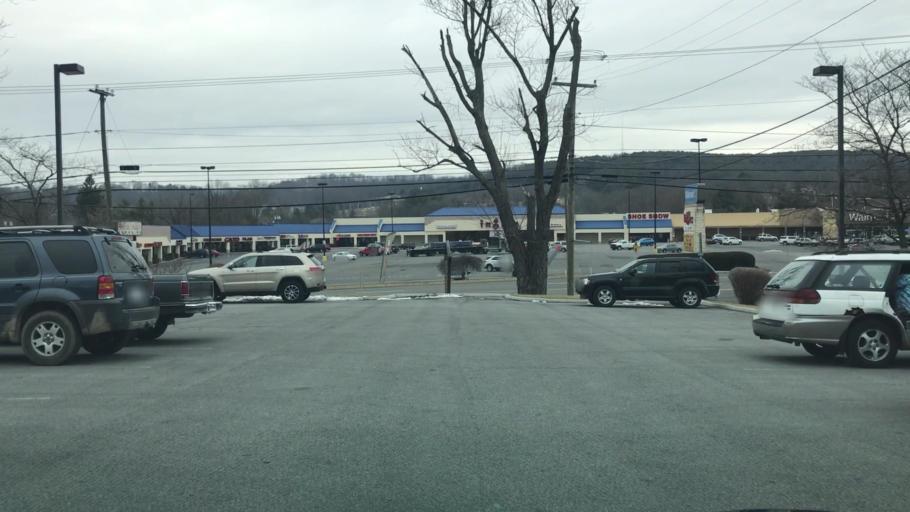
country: US
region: Virginia
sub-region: Smyth County
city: Marion
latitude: 36.8441
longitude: -81.5006
